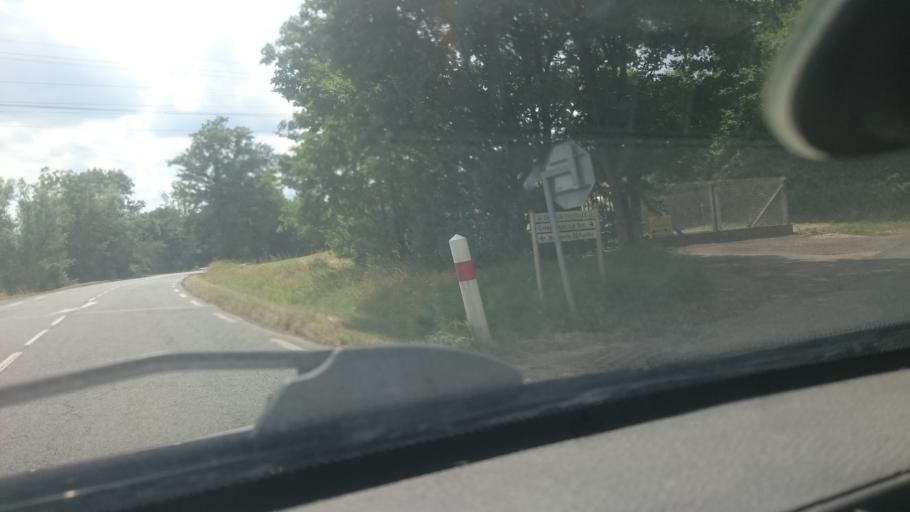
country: FR
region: Rhone-Alpes
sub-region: Departement du Rhone
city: Lozanne
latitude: 45.8579
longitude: 4.6555
